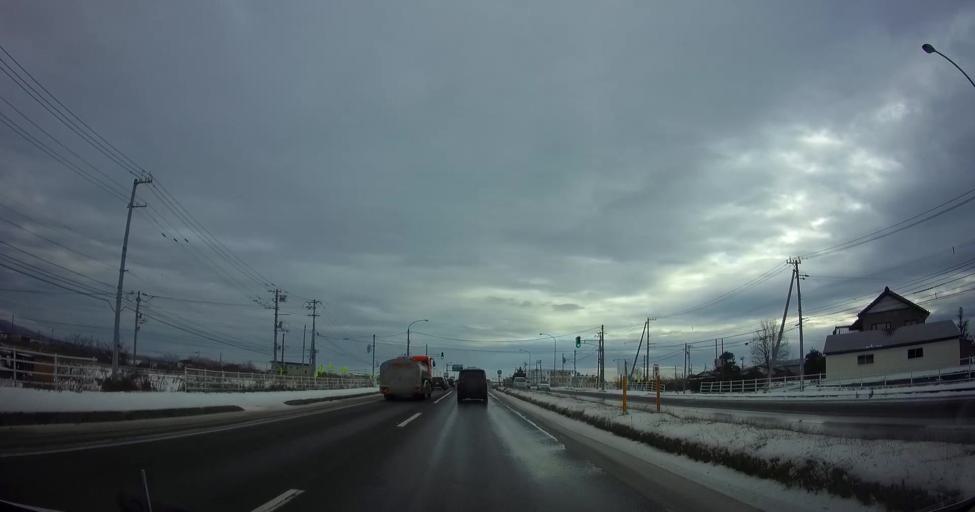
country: JP
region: Hokkaido
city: Nanae
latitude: 41.8393
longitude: 140.6895
